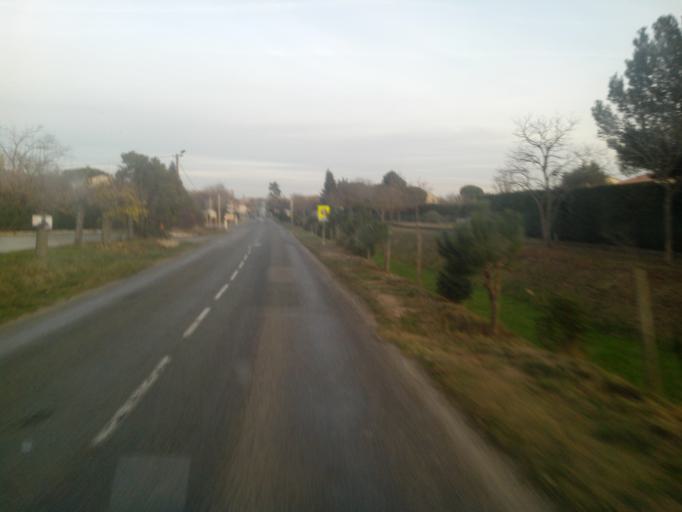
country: FR
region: Languedoc-Roussillon
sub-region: Departement de l'Aude
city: Puicheric
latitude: 43.2226
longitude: 2.6178
